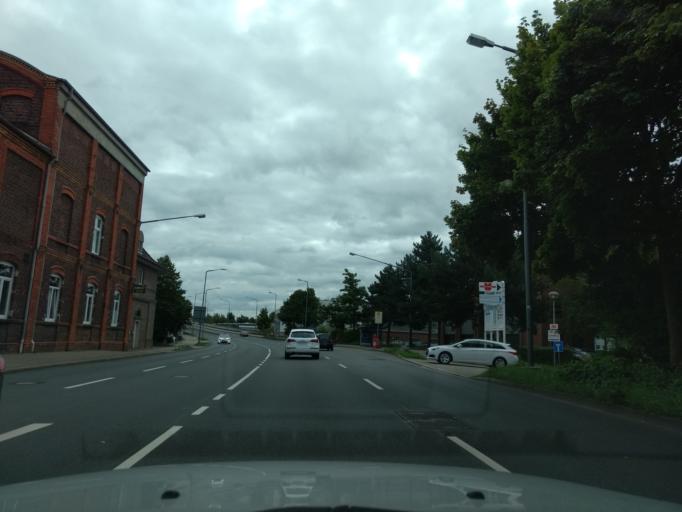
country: DE
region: North Rhine-Westphalia
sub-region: Regierungsbezirk Dusseldorf
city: Ratingen
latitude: 51.2983
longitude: 6.8327
